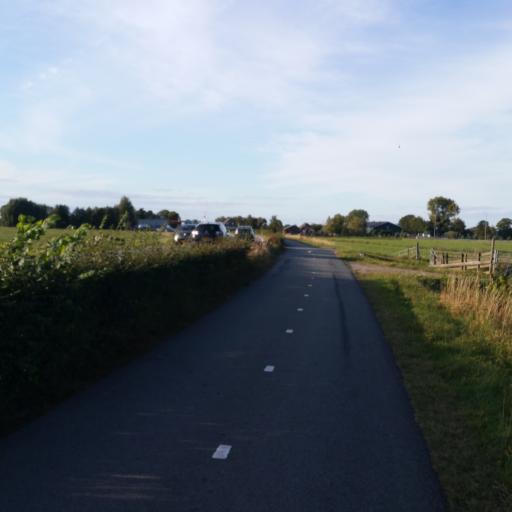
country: NL
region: Utrecht
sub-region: Gemeente Lopik
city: Lopik
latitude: 52.0013
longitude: 4.9652
